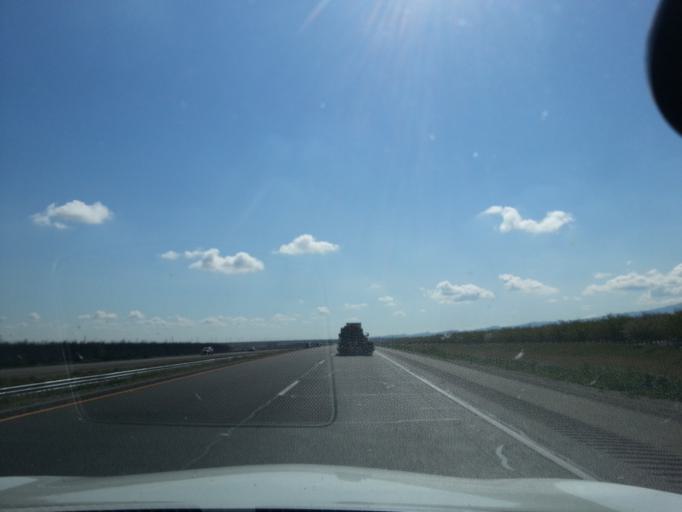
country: US
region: California
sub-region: Fresno County
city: San Joaquin
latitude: 36.4489
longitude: -120.4063
